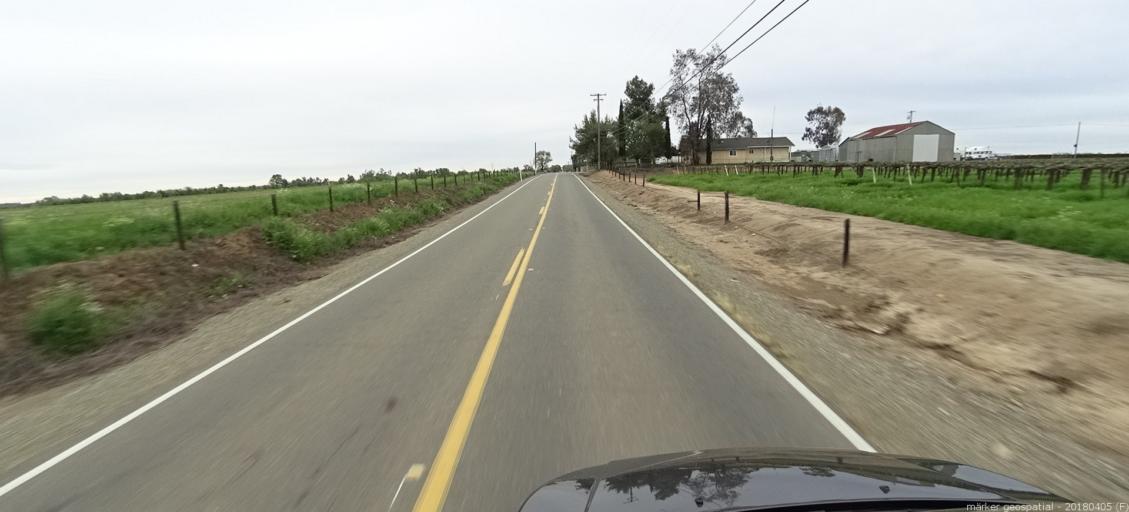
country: US
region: California
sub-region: Sacramento County
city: Herald
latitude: 38.3188
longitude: -121.2263
